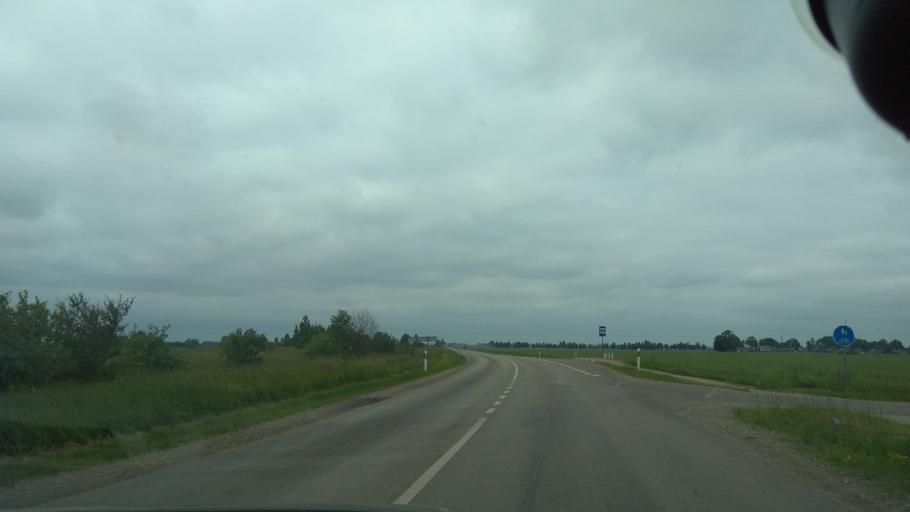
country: LT
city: Linkuva
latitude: 56.0322
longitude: 23.9485
